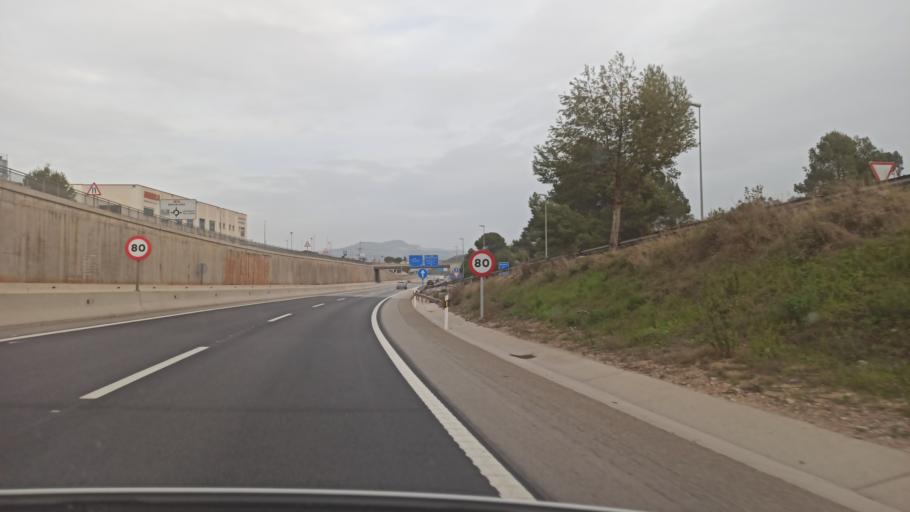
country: ES
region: Catalonia
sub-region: Provincia de Barcelona
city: Cervello
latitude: 41.3977
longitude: 1.9722
